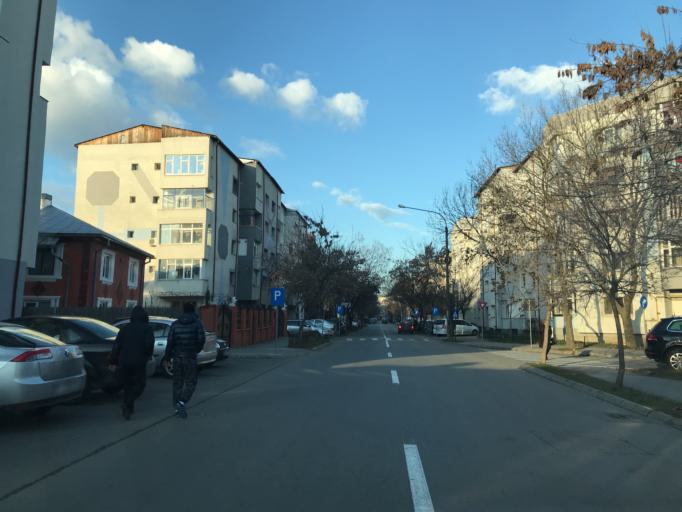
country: RO
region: Olt
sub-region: Municipiul Slatina
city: Slatina
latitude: 44.4182
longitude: 24.3808
